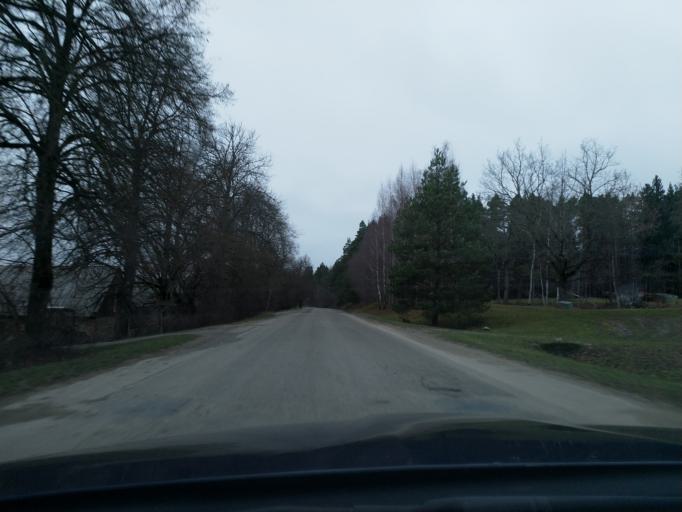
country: LV
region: Ventspils Rajons
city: Piltene
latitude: 57.1235
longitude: 21.8108
